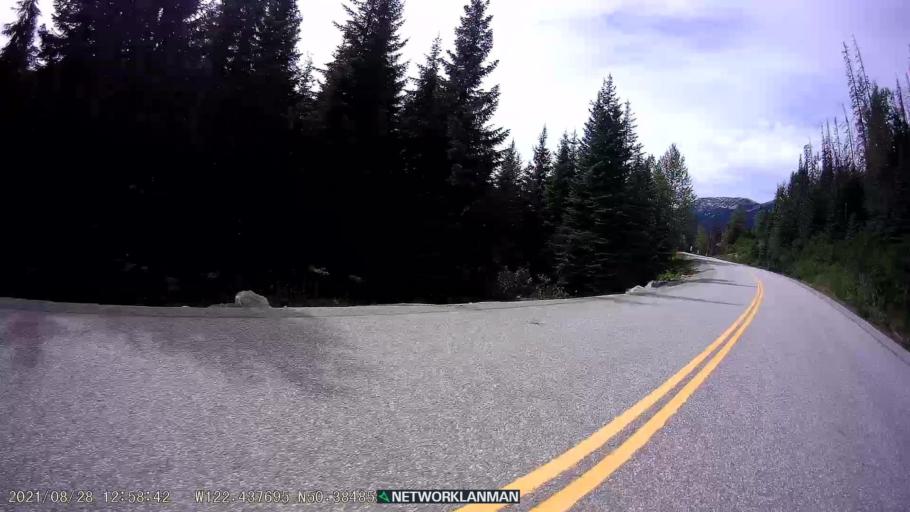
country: CA
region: British Columbia
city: Pemberton
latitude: 50.3845
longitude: -122.4383
